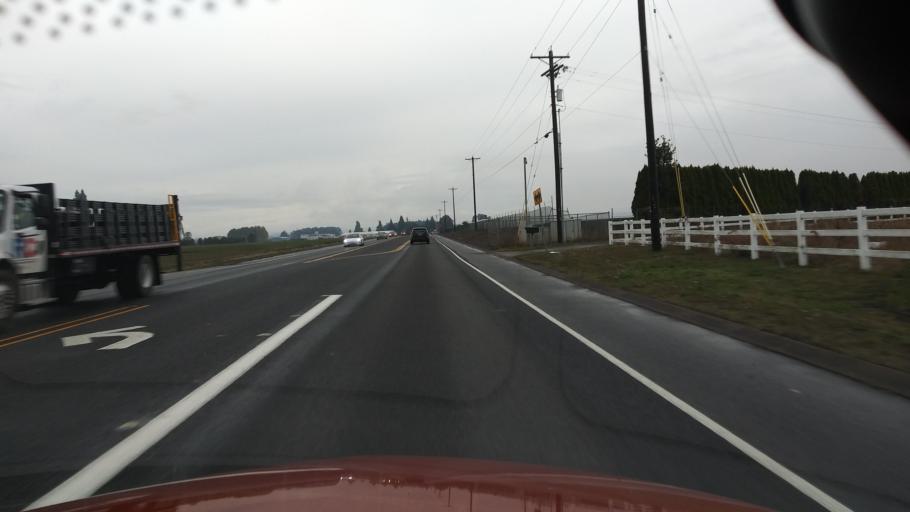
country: US
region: Oregon
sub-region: Washington County
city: Cornelius
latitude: 45.5632
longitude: -123.0539
